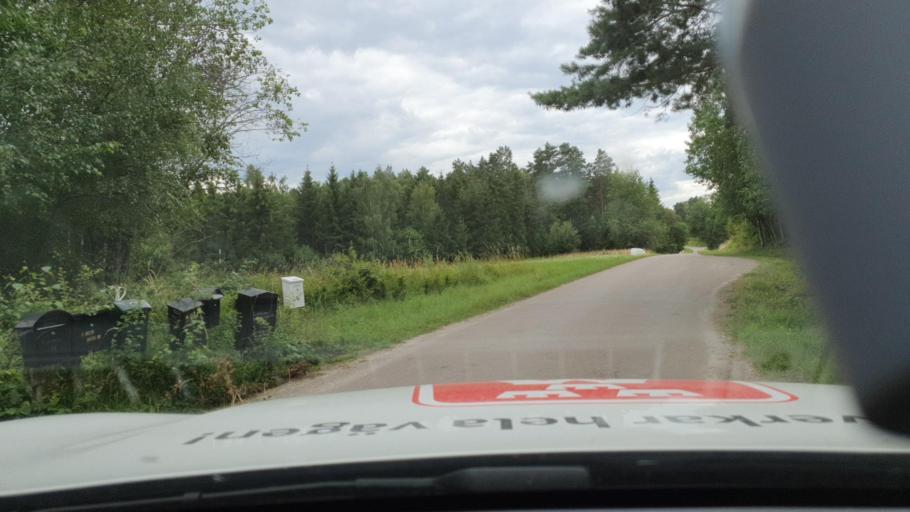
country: SE
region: Soedermanland
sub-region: Strangnas Kommun
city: Stallarholmen
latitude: 59.4070
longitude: 17.3073
